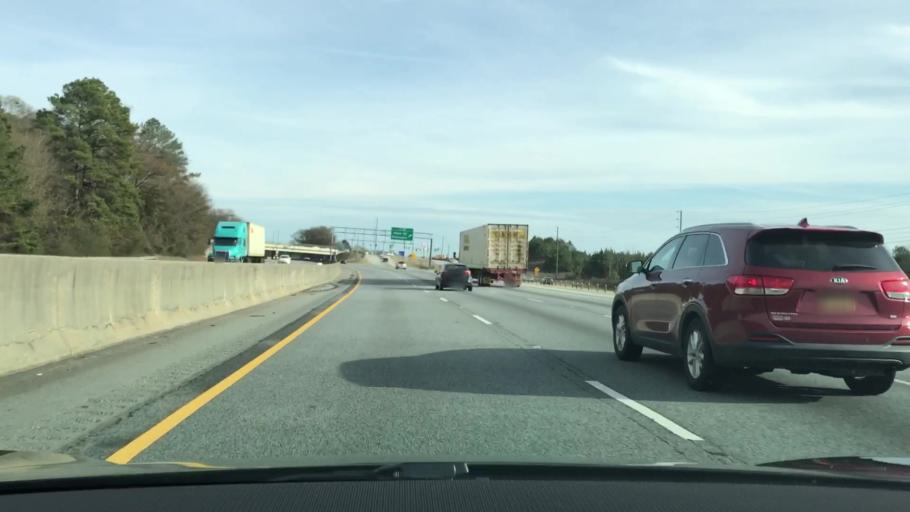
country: US
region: Georgia
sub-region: Newton County
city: Porterdale
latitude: 33.6169
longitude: -83.9254
